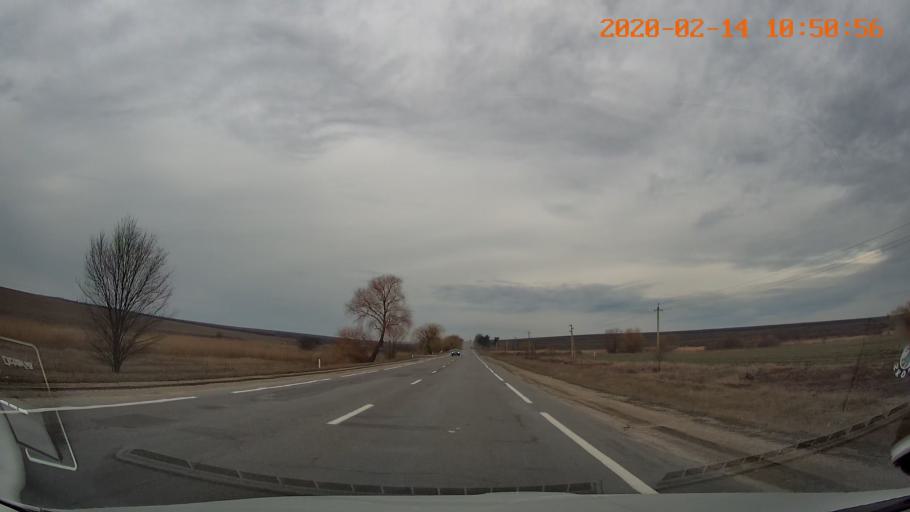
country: MD
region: Riscani
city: Riscani
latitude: 48.0861
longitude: 27.4656
